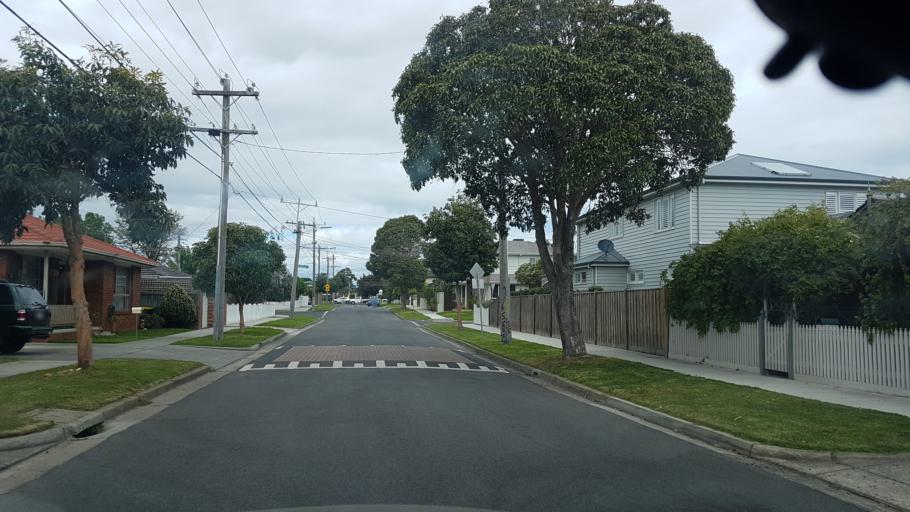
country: AU
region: Victoria
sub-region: Bayside
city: Moorabbin
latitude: -37.9324
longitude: 145.0439
